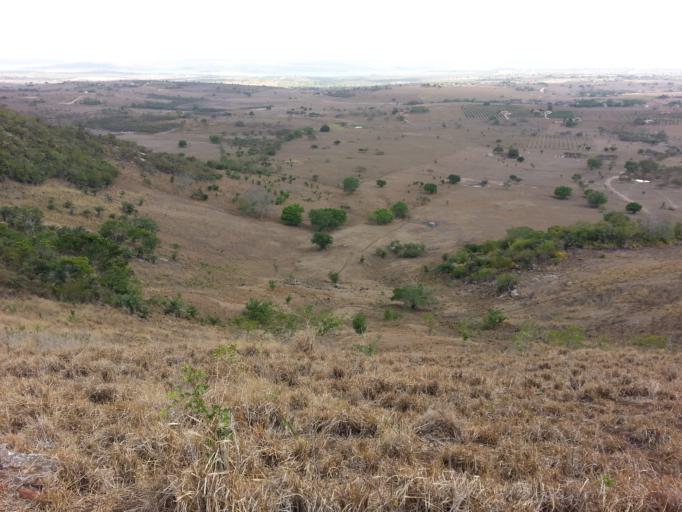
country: BR
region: Bahia
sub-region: Cruz Das Almas
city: Cruz das Almas
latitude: -12.5991
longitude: -39.1930
